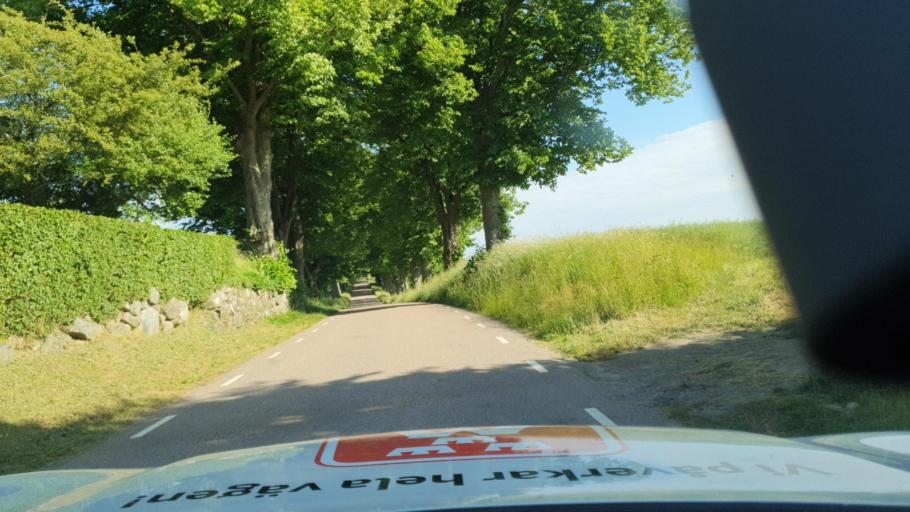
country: SE
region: Skane
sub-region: Skurups Kommun
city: Rydsgard
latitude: 55.4289
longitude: 13.6912
